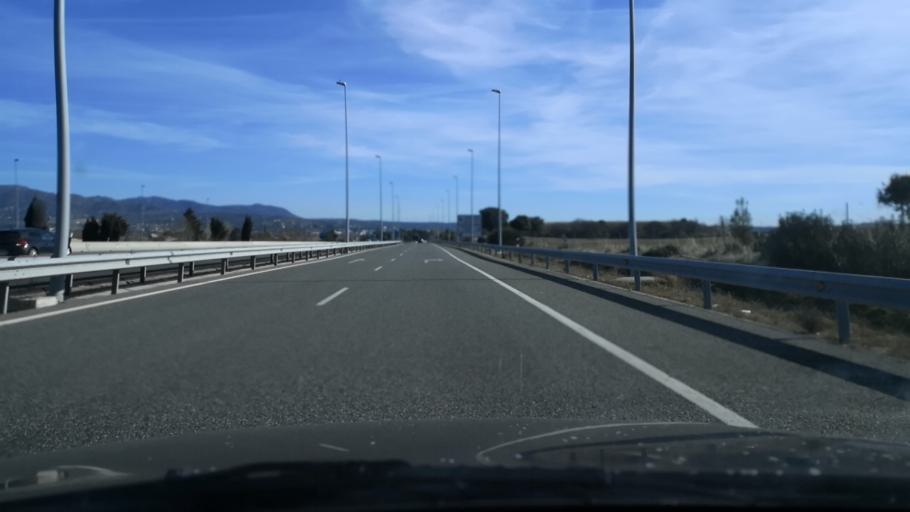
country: ES
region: Madrid
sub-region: Provincia de Madrid
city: Alpedrete
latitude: 40.6447
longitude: -4.0470
